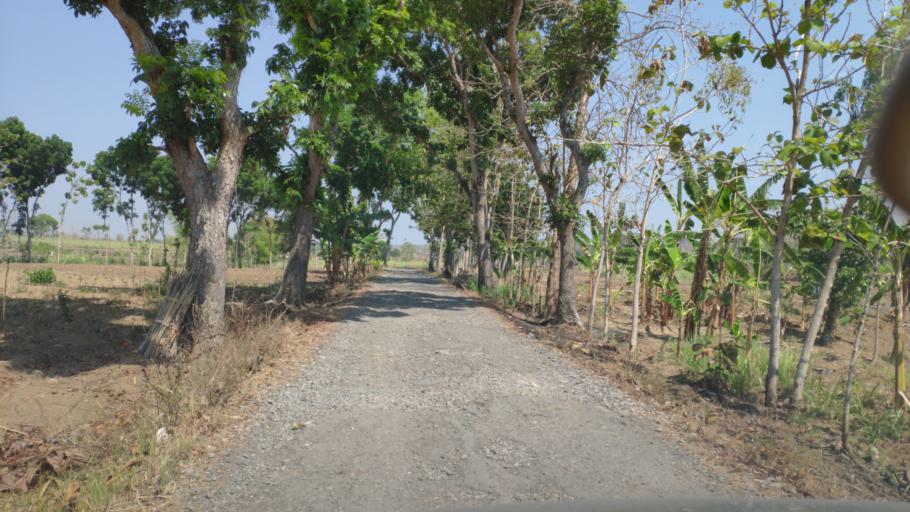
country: ID
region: Central Java
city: Ngundaan
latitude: -6.9214
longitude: 111.3977
